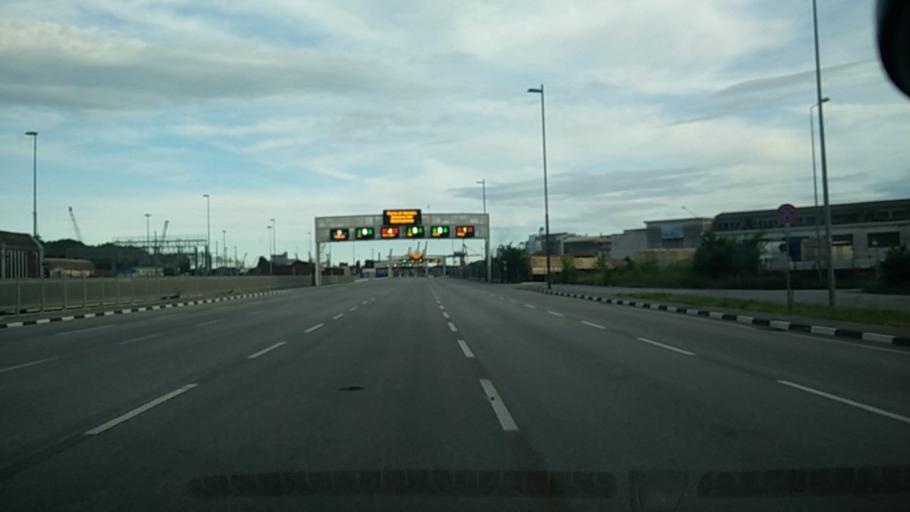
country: IT
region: Veneto
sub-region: Provincia di Venezia
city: Mestre
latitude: 45.4659
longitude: 12.2398
